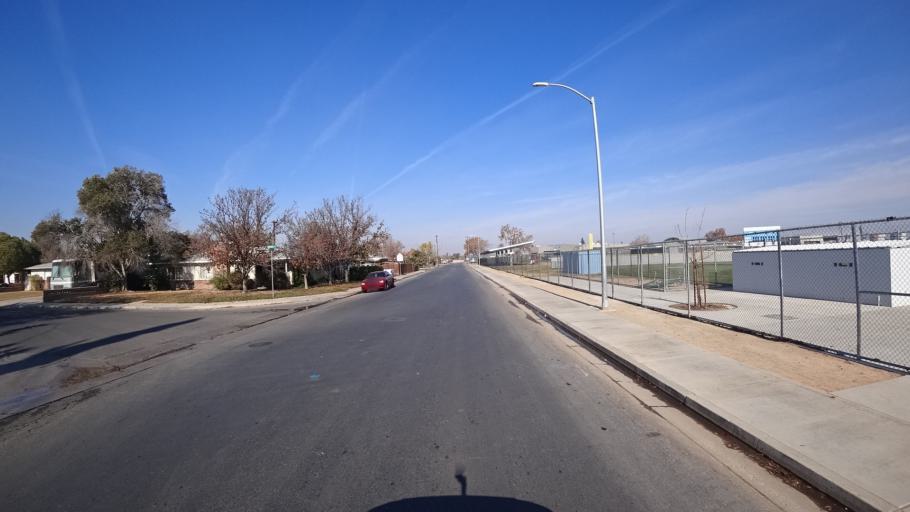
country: US
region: California
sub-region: Kern County
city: Bakersfield
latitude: 35.3215
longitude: -119.0163
